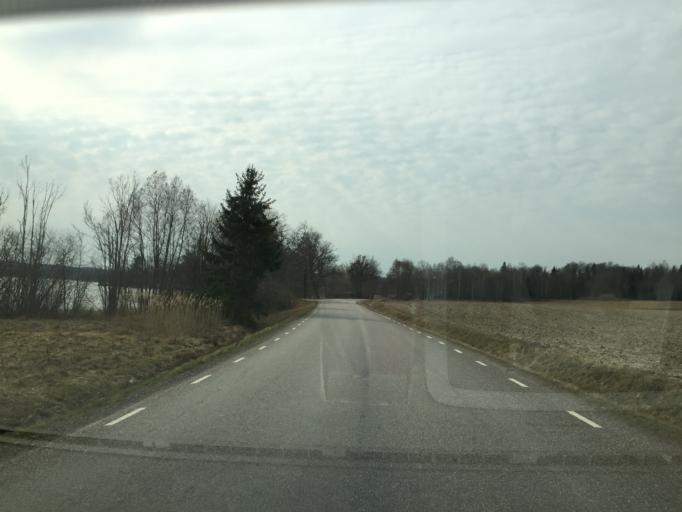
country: SE
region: Soedermanland
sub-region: Vingakers Kommun
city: Vingaker
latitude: 59.0355
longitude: 15.6985
